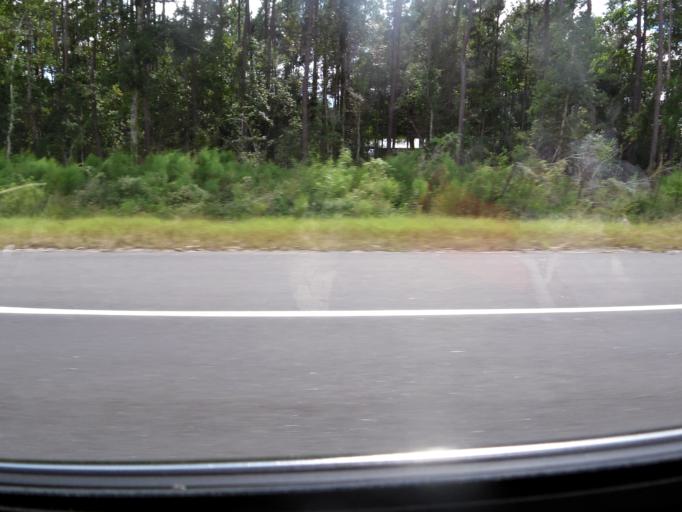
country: US
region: Georgia
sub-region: Glynn County
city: Dock Junction
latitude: 31.1916
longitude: -81.6604
